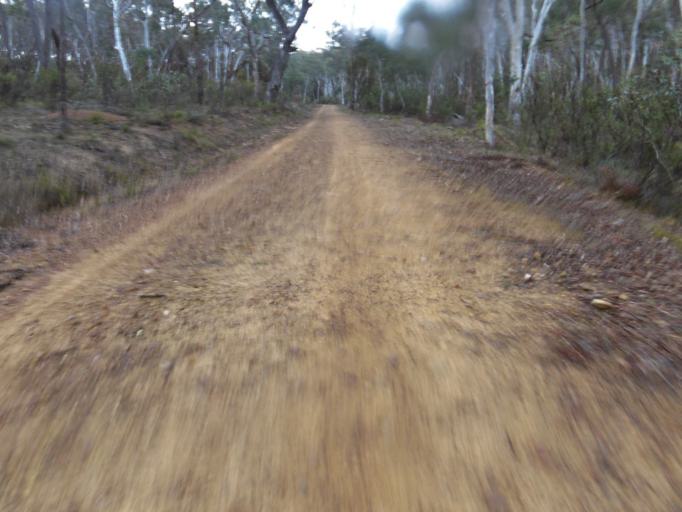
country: AU
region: Australian Capital Territory
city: Acton
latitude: -35.2659
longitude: 149.0919
